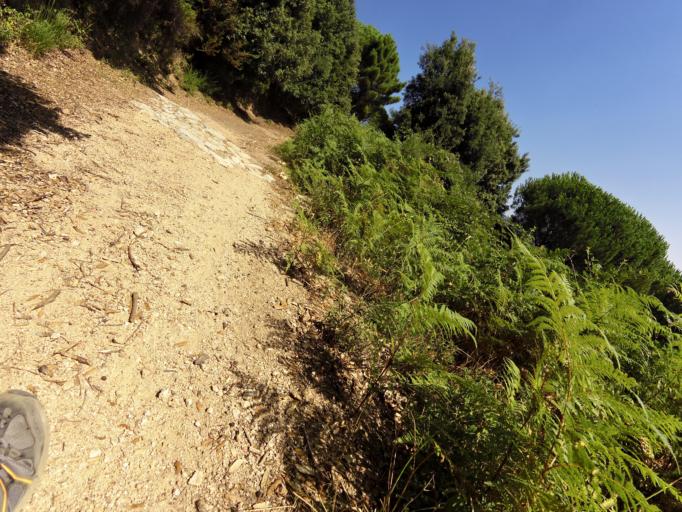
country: IT
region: Calabria
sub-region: Provincia di Reggio Calabria
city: Bivongi
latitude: 38.5064
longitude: 16.4369
